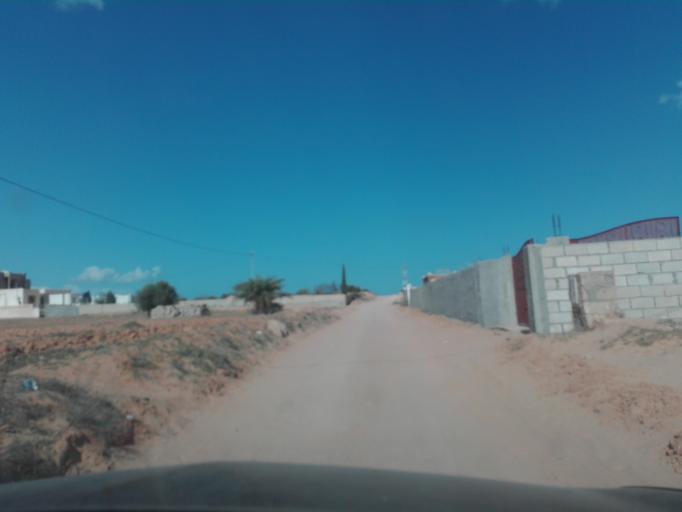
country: TN
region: Madanin
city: Bin Qirdan
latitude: 33.1632
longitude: 11.1956
